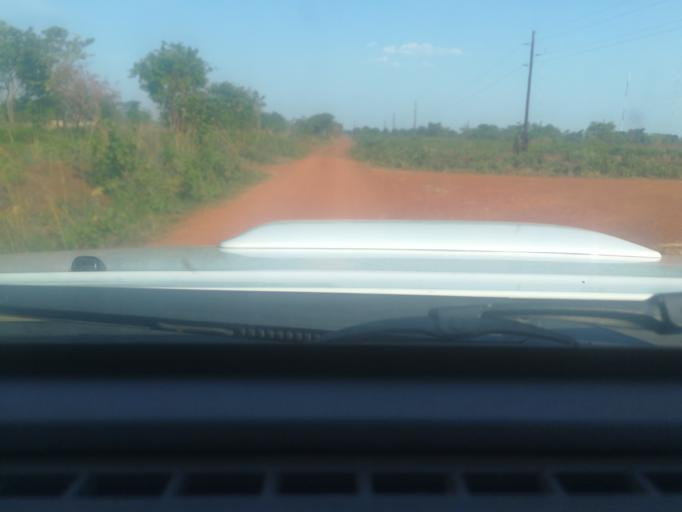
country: ZM
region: Northern
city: Kasama
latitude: -10.2141
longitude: 31.1373
